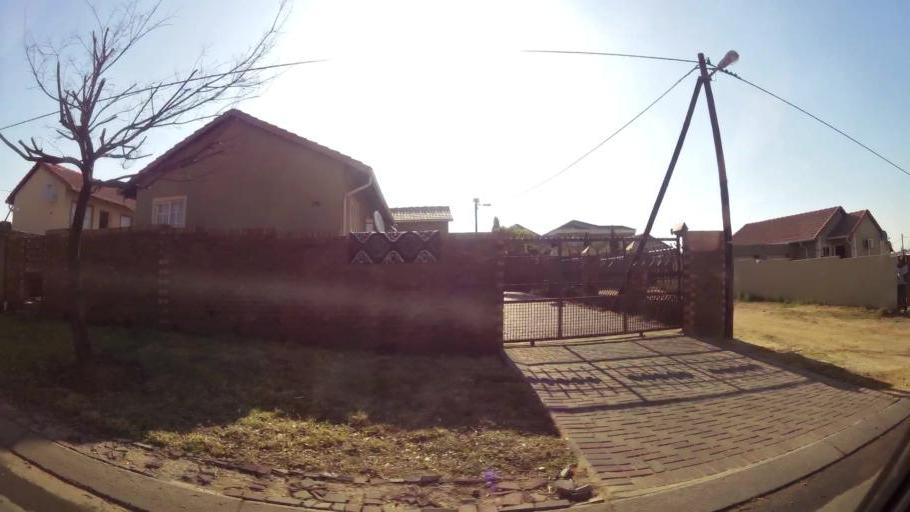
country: ZA
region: Gauteng
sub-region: West Rand District Municipality
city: Muldersdriseloop
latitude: -26.0334
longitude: 27.9190
